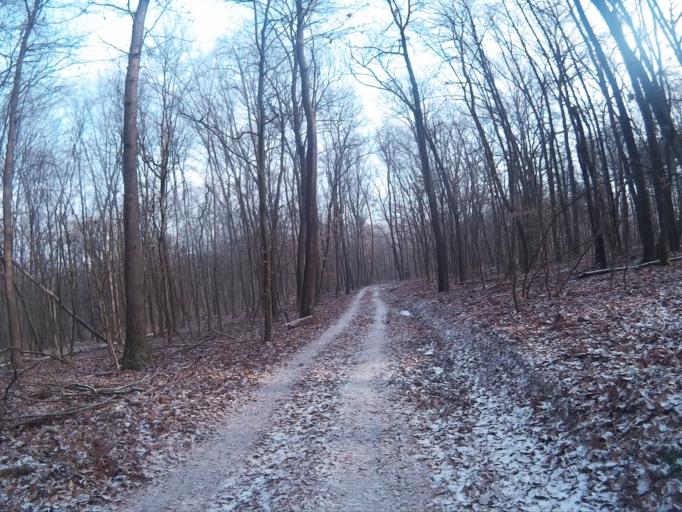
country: HU
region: Borsod-Abauj-Zemplen
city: Szendro
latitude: 48.4950
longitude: 20.7753
